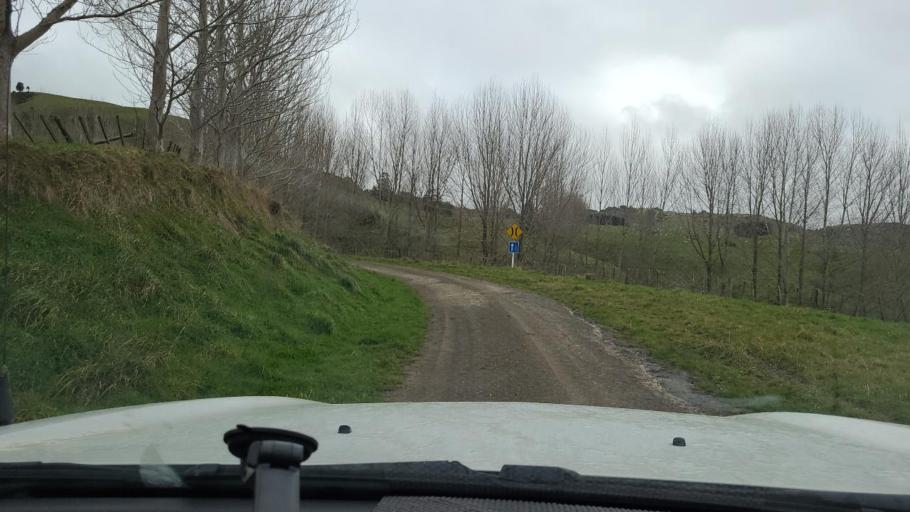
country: NZ
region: Hawke's Bay
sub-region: Wairoa District
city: Wairoa
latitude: -38.5413
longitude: 177.4182
